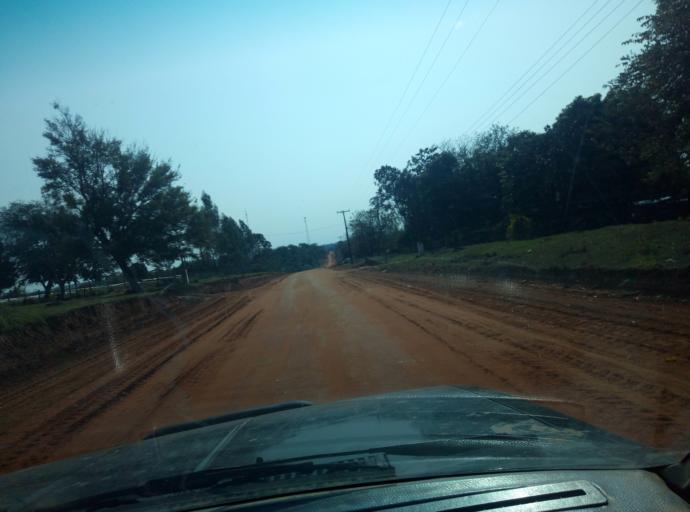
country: PY
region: Caaguazu
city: Carayao
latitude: -25.3219
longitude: -56.3293
